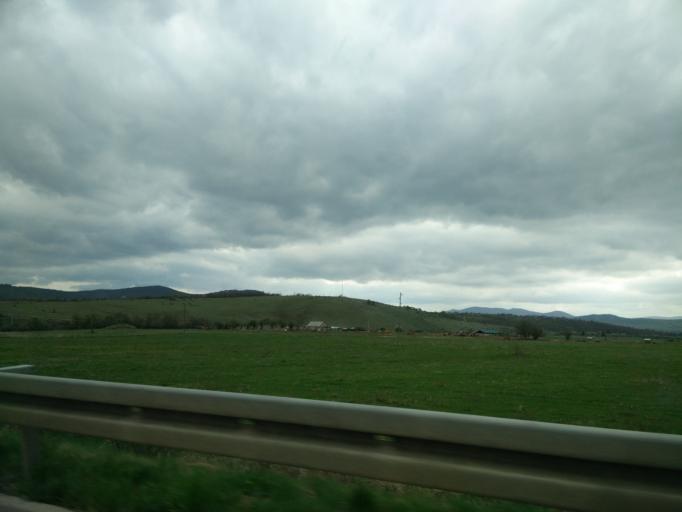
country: HR
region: Zadarska
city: Gracac
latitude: 44.5391
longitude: 15.7525
